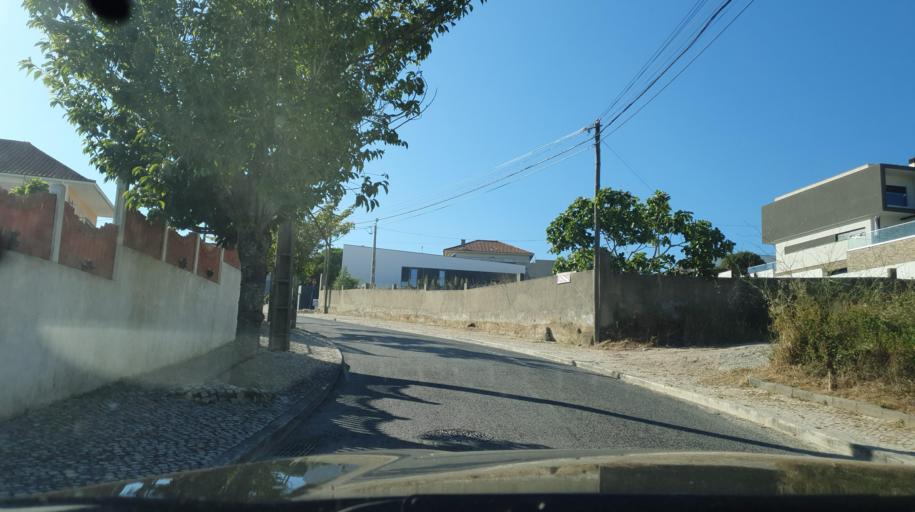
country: PT
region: Lisbon
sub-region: Sintra
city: Belas
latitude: 38.7967
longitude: -9.2506
